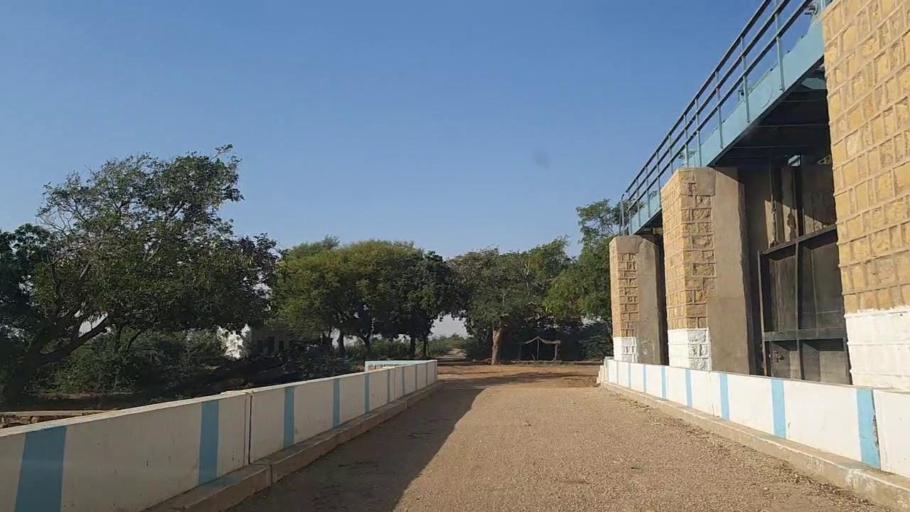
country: PK
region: Sindh
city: Daro Mehar
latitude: 25.0393
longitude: 68.1366
